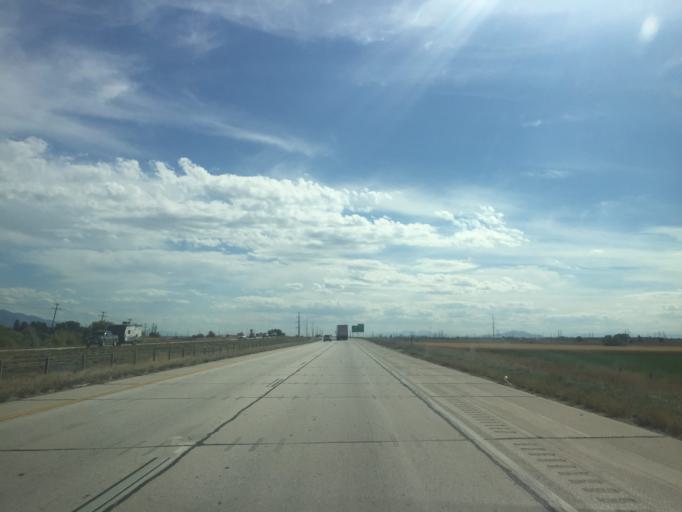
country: US
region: Utah
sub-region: Box Elder County
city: South Willard
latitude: 41.3622
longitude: -112.0434
